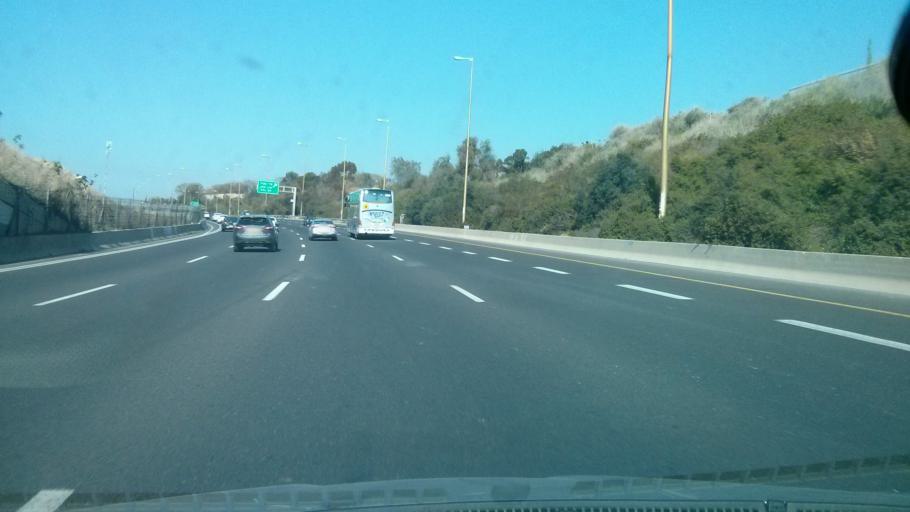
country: IL
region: Tel Aviv
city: Ramat Gan
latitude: 32.1131
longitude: 34.8109
